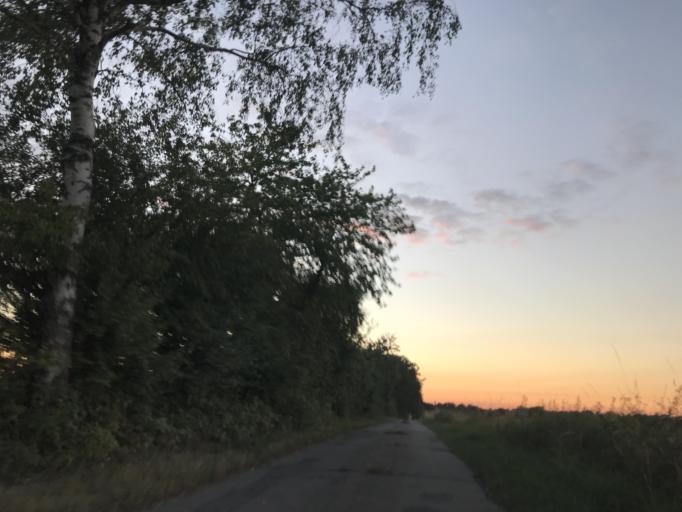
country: DE
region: Lower Saxony
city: Reinstorf
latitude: 53.2267
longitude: 10.5970
